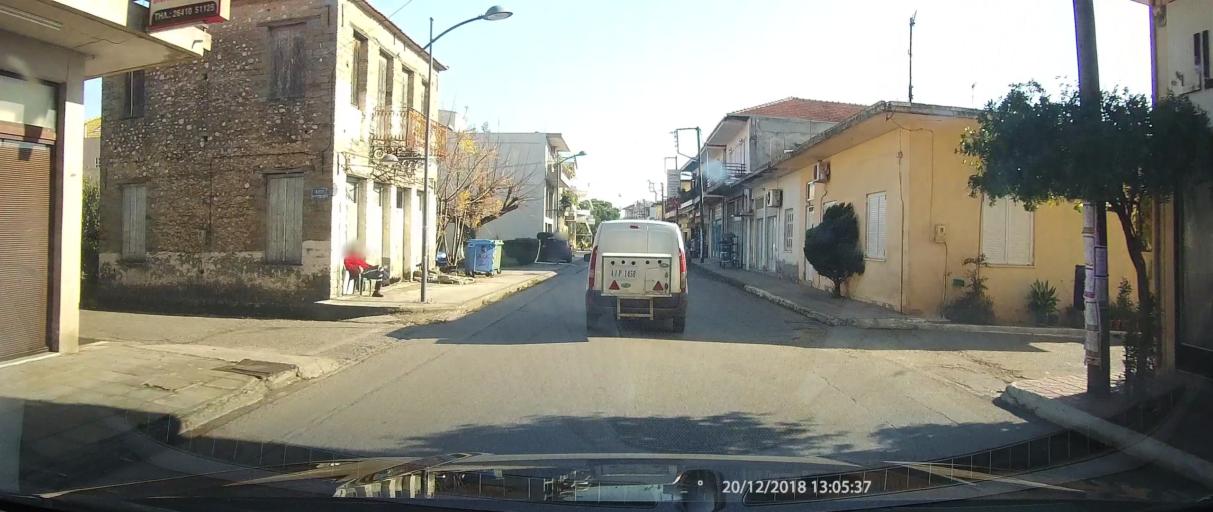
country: GR
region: West Greece
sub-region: Nomos Aitolias kai Akarnanias
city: Panaitolion
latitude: 38.5832
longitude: 21.4435
